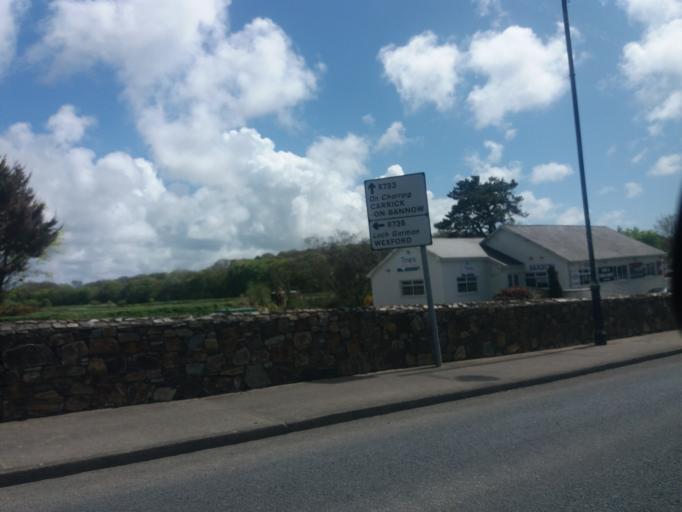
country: IE
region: Leinster
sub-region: Loch Garman
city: New Ross
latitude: 52.2674
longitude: -6.7510
